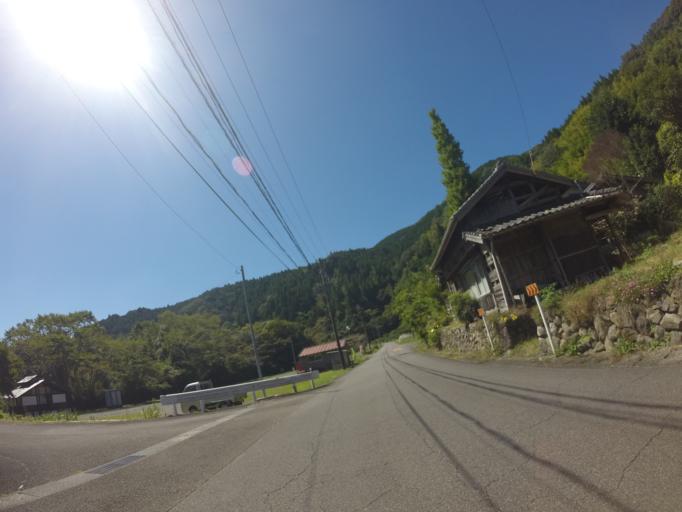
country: JP
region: Shizuoka
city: Fujieda
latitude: 34.9570
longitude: 138.2100
